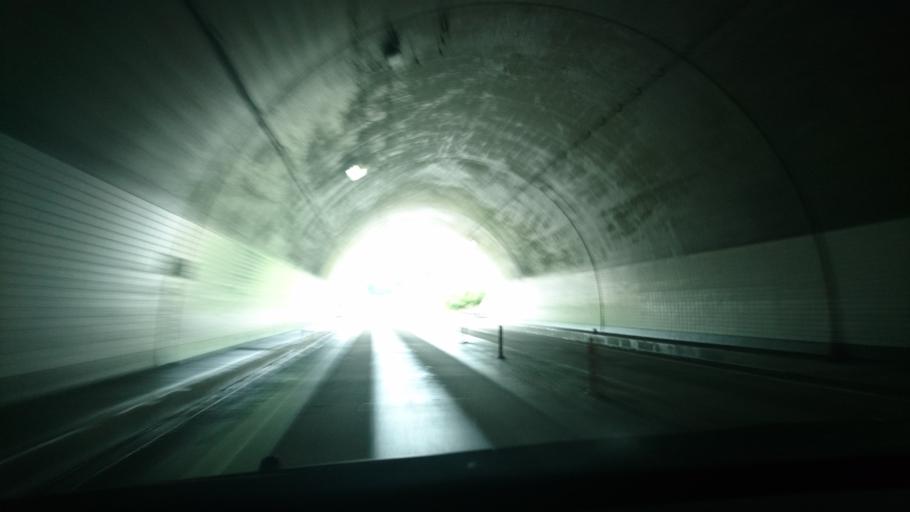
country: JP
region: Iwate
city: Miyako
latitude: 40.0121
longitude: 141.8882
